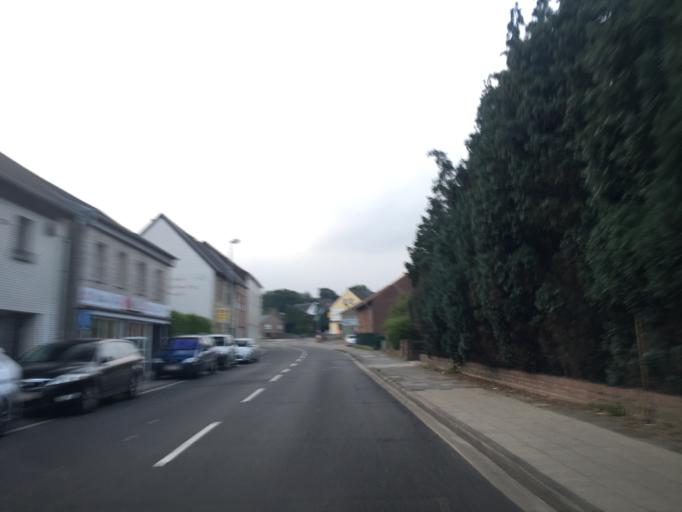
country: DE
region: North Rhine-Westphalia
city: Huckelhoven
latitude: 51.0549
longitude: 6.2293
